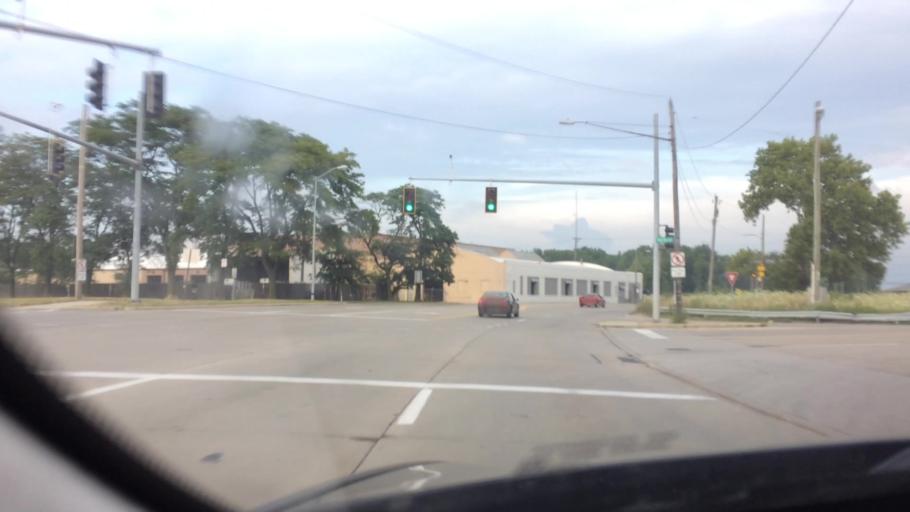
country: US
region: Ohio
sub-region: Wood County
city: Rossford
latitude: 41.6386
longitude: -83.5931
